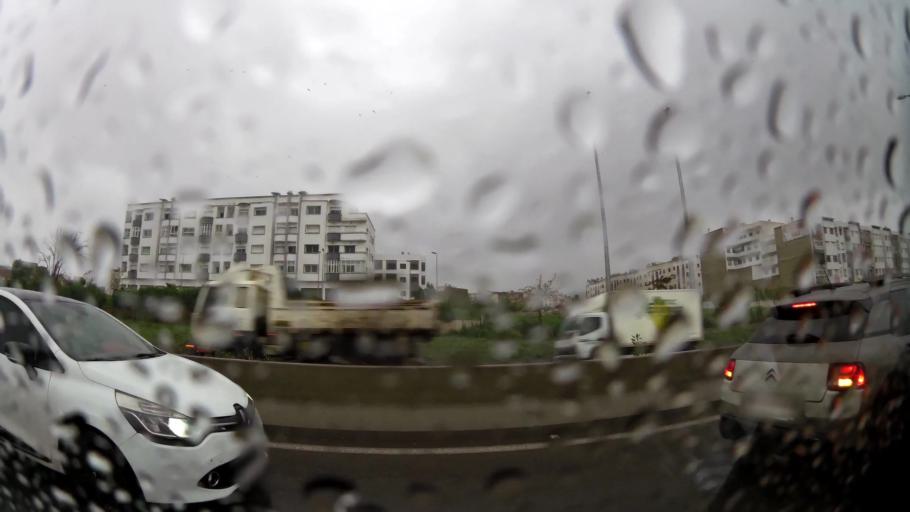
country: MA
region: Grand Casablanca
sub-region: Mediouna
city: Tit Mellil
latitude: 33.5977
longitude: -7.5136
